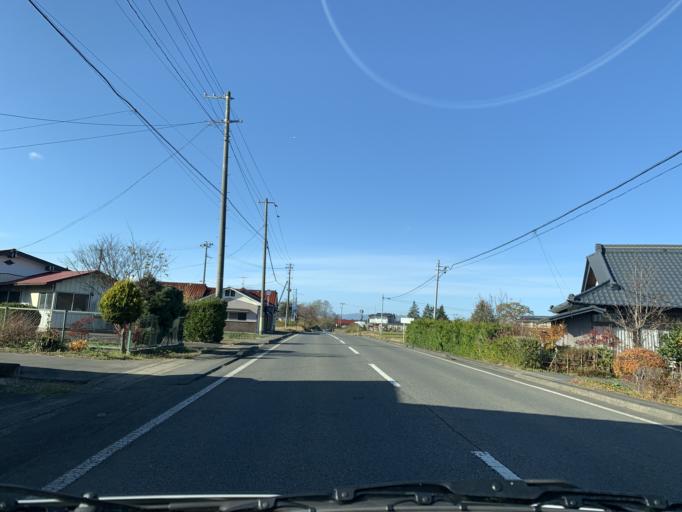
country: JP
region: Iwate
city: Mizusawa
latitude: 39.1822
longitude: 141.1308
